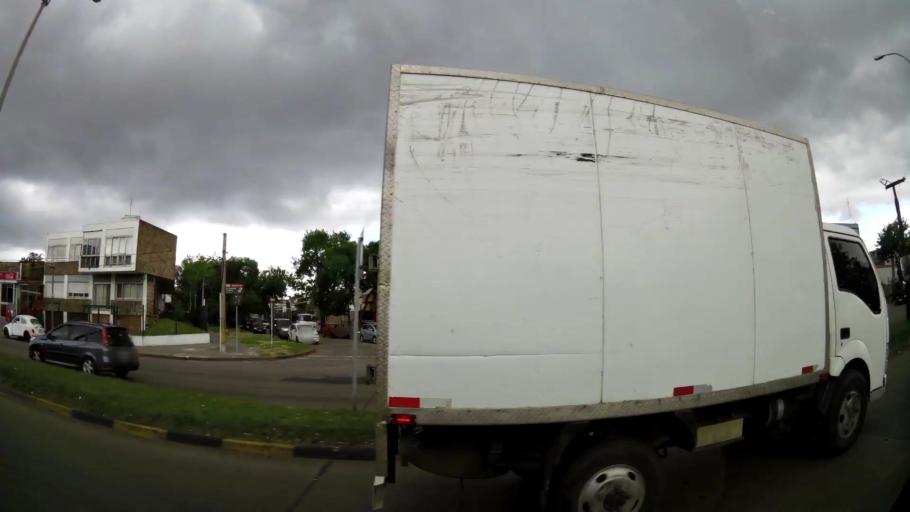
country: UY
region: Montevideo
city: Montevideo
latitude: -34.8684
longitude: -56.1620
